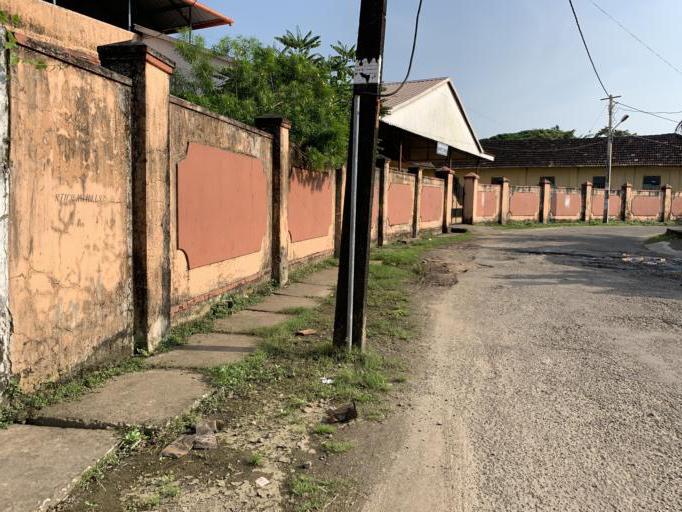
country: IN
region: Kerala
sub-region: Ernakulam
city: Cochin
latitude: 9.9590
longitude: 76.2515
